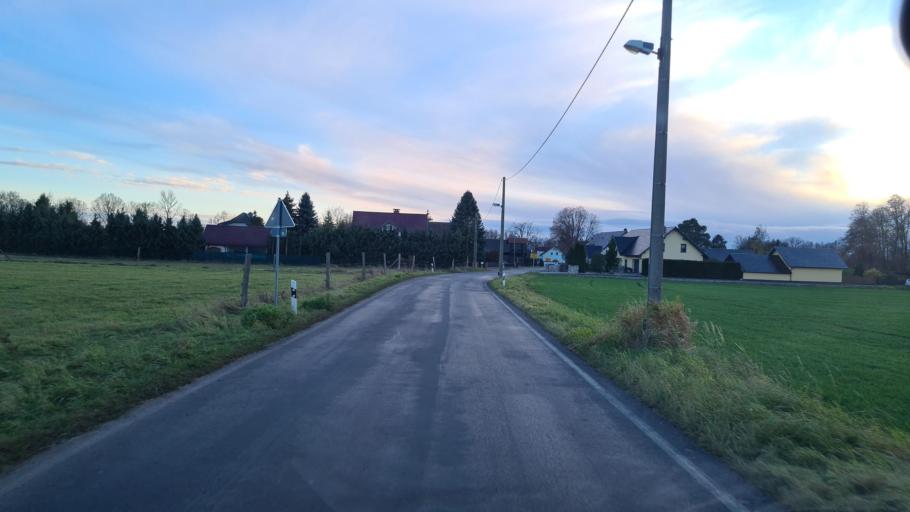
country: DE
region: Brandenburg
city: Burg
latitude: 51.7955
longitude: 14.1447
